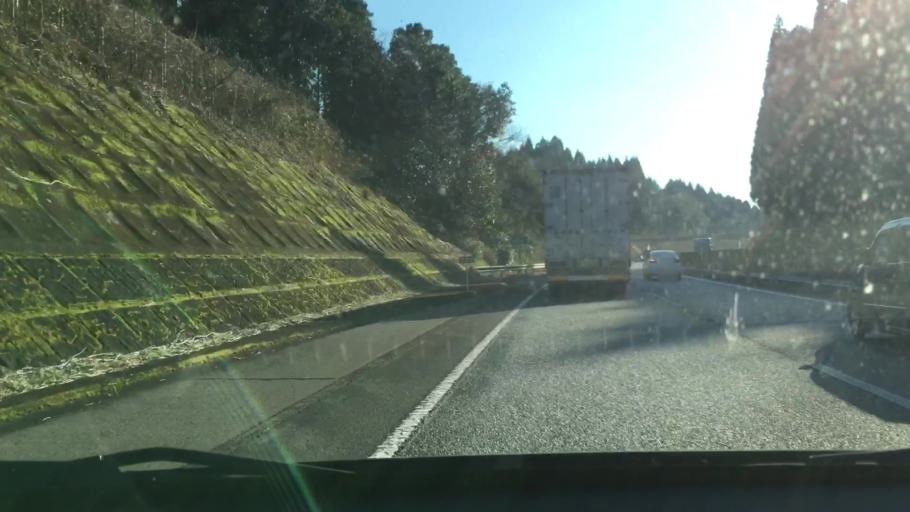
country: JP
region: Kagoshima
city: Kajiki
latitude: 31.8744
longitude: 130.6944
